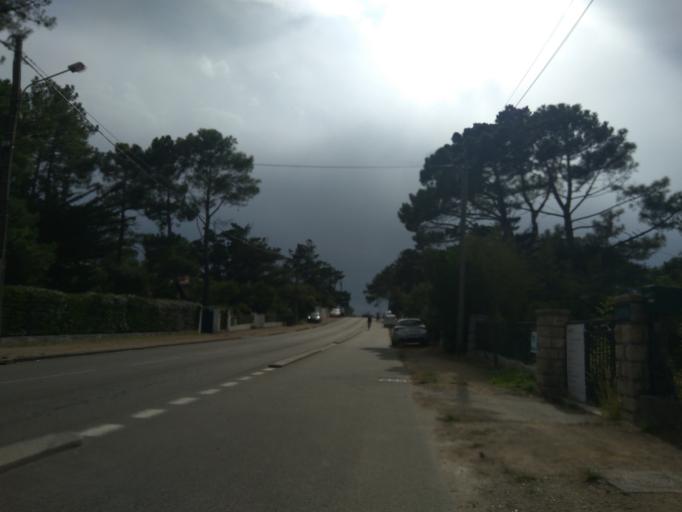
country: FR
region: Aquitaine
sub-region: Departement des Landes
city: Capbreton
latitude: 43.6455
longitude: -1.4405
